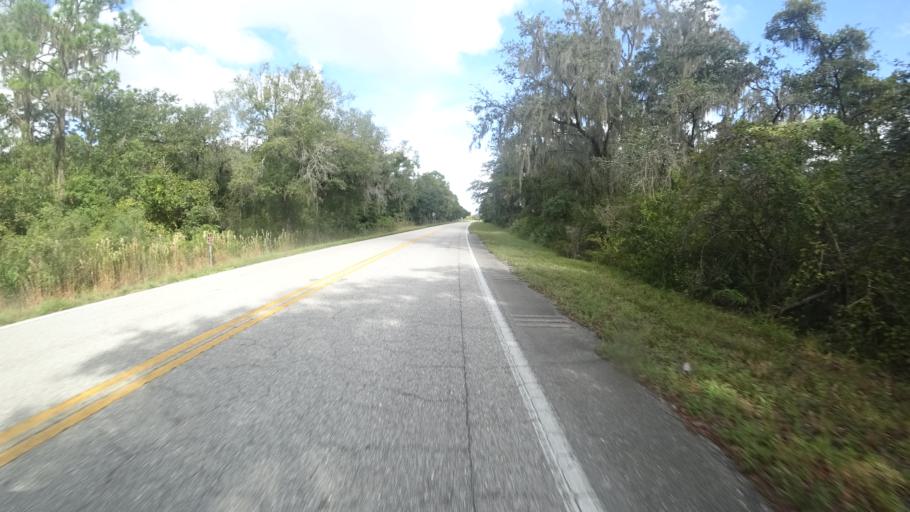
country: US
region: Florida
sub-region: Hillsborough County
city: Wimauma
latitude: 27.5400
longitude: -82.1038
